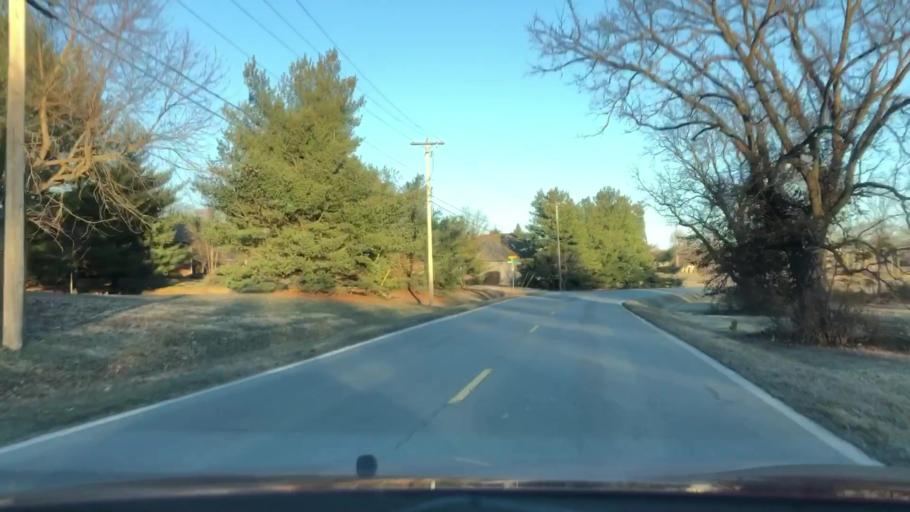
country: US
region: Missouri
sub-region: Greene County
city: Springfield
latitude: 37.1658
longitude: -93.2460
